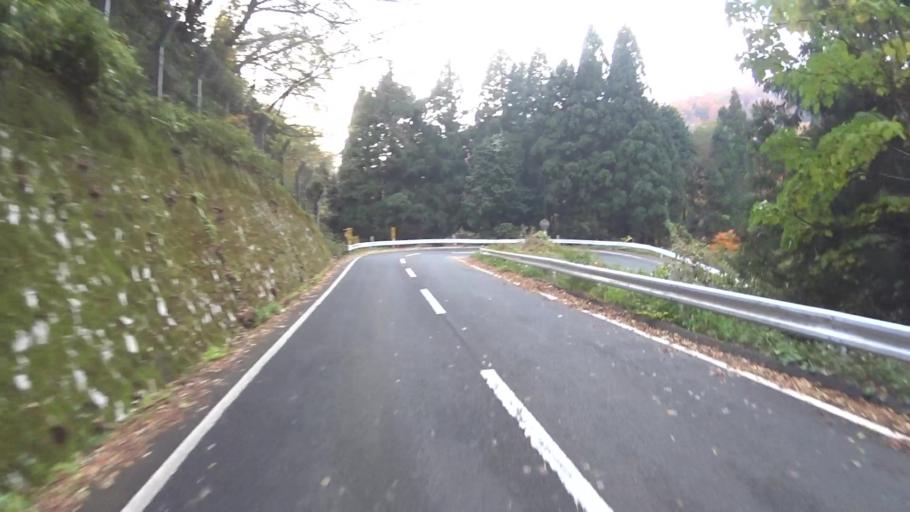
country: JP
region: Kyoto
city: Maizuru
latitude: 35.5387
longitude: 135.4505
